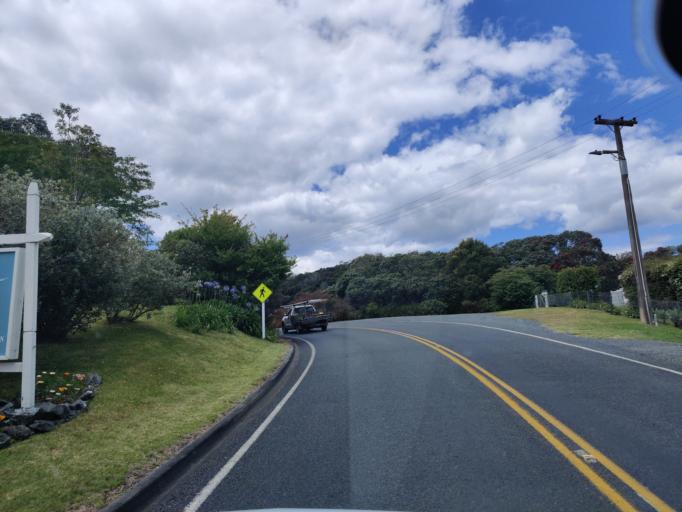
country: NZ
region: Northland
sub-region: Far North District
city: Paihia
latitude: -35.2666
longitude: 174.1261
